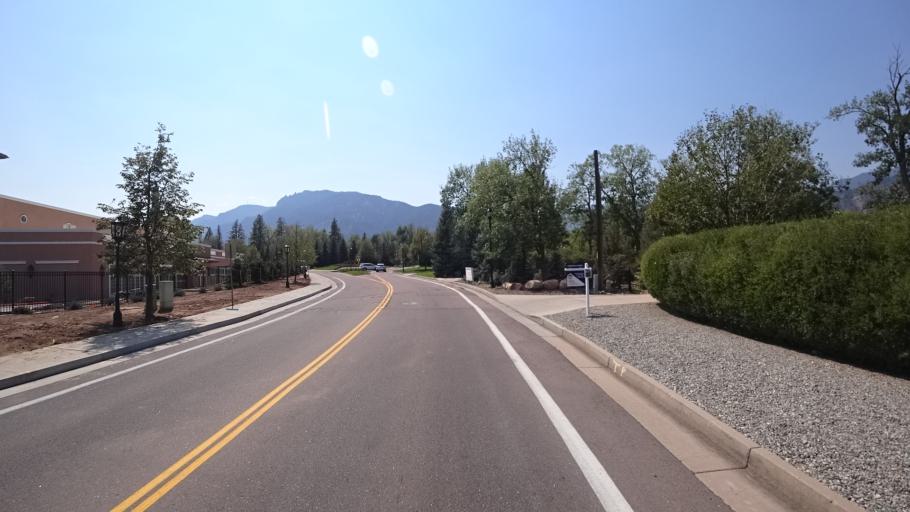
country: US
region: Colorado
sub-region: El Paso County
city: Colorado Springs
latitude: 38.7942
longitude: -104.8517
